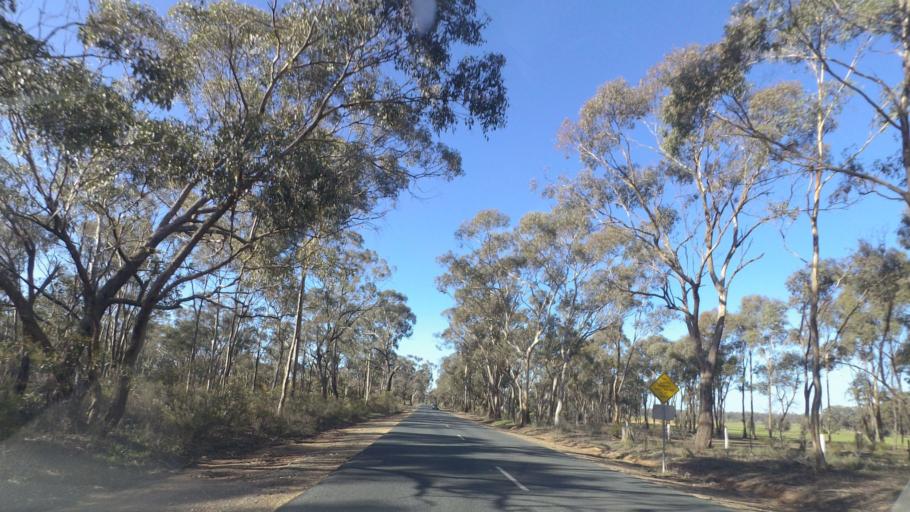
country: AU
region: Victoria
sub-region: Greater Bendigo
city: Epsom
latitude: -36.6630
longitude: 144.4505
